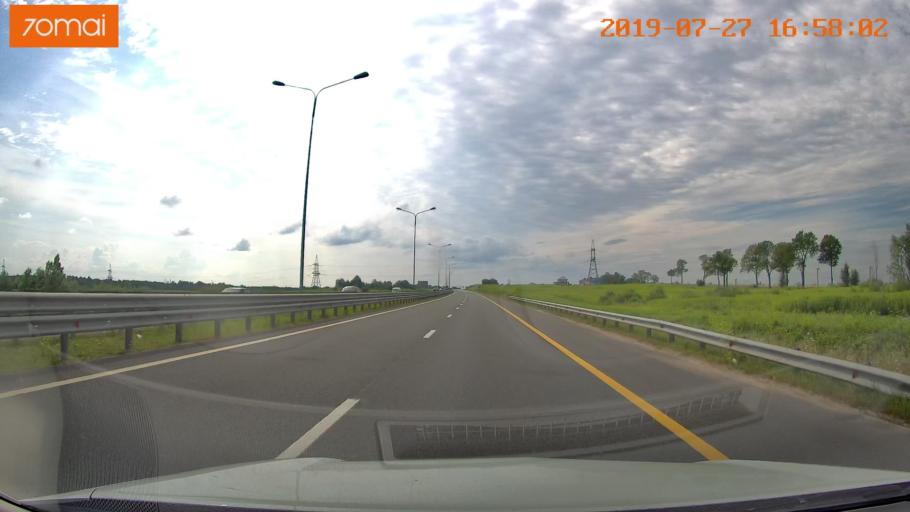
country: RU
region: Kaliningrad
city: Bol'shoe Isakovo
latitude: 54.7012
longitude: 20.6940
